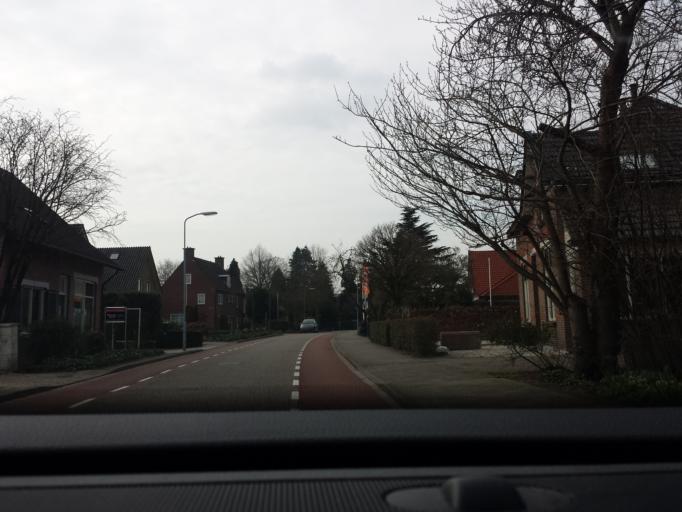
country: NL
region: Gelderland
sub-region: Gemeente Bronckhorst
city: Zelhem
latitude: 52.0059
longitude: 6.3542
